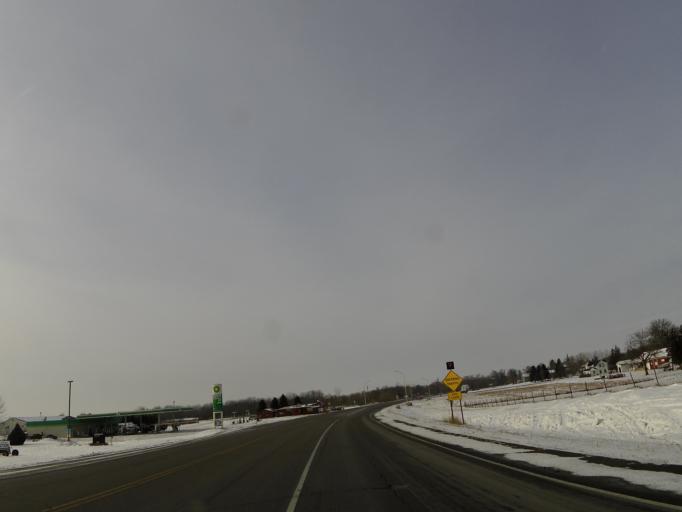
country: US
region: Minnesota
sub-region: McLeod County
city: Lester Prairie
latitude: 44.9050
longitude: -93.9675
